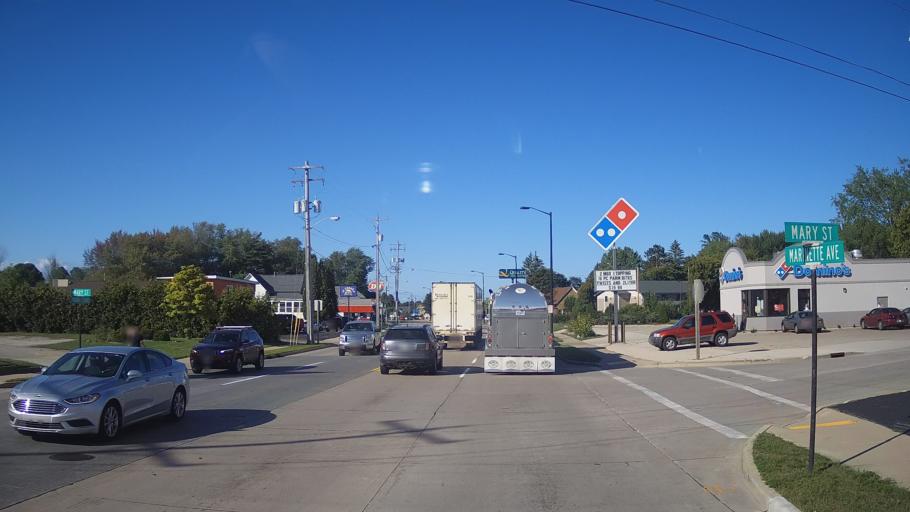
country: US
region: Wisconsin
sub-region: Marinette County
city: Marinette
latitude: 45.0892
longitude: -87.6500
